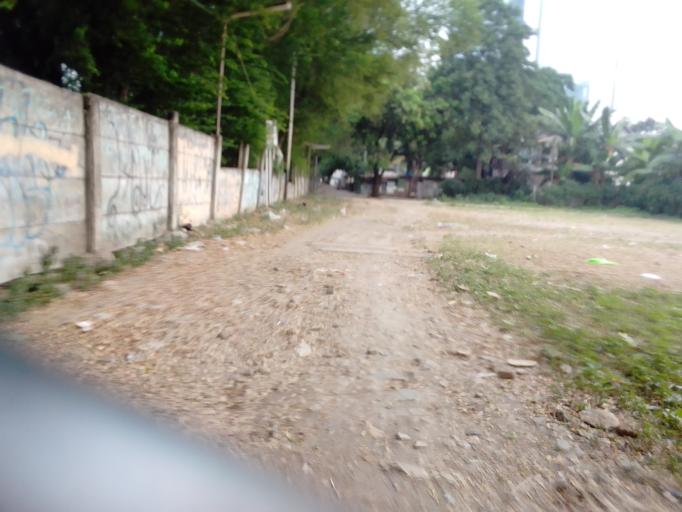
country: ID
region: Jakarta Raya
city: Jakarta
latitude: -6.1995
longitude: 106.8177
